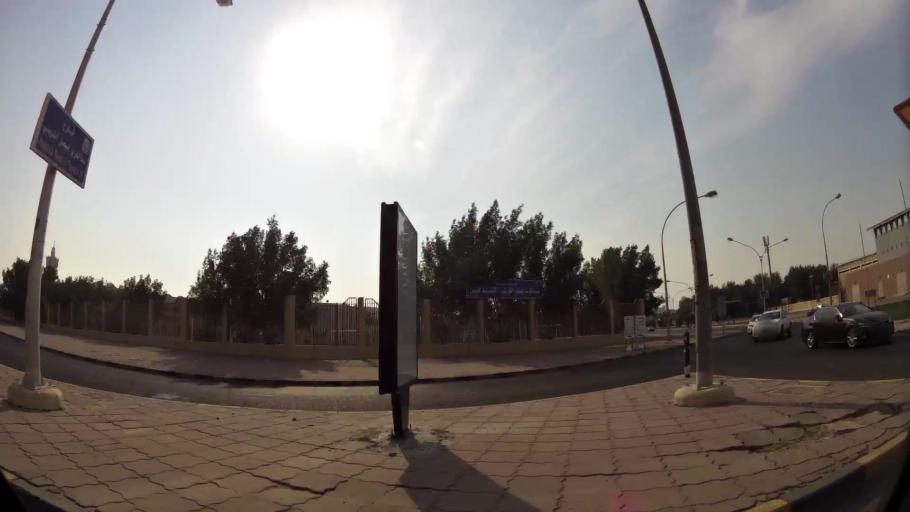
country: KW
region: Al Farwaniyah
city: Janub as Surrah
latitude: 29.3102
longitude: 47.9888
